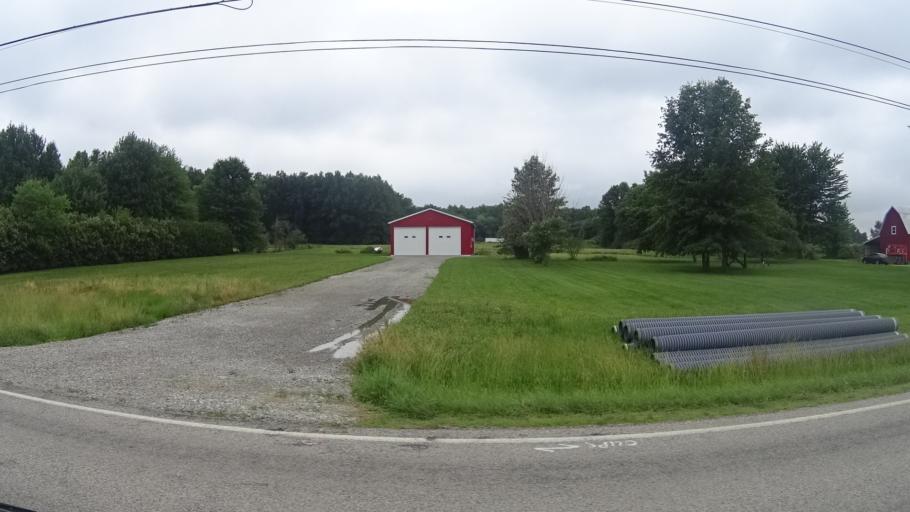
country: US
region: Ohio
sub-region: Erie County
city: Huron
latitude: 41.3307
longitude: -82.5101
